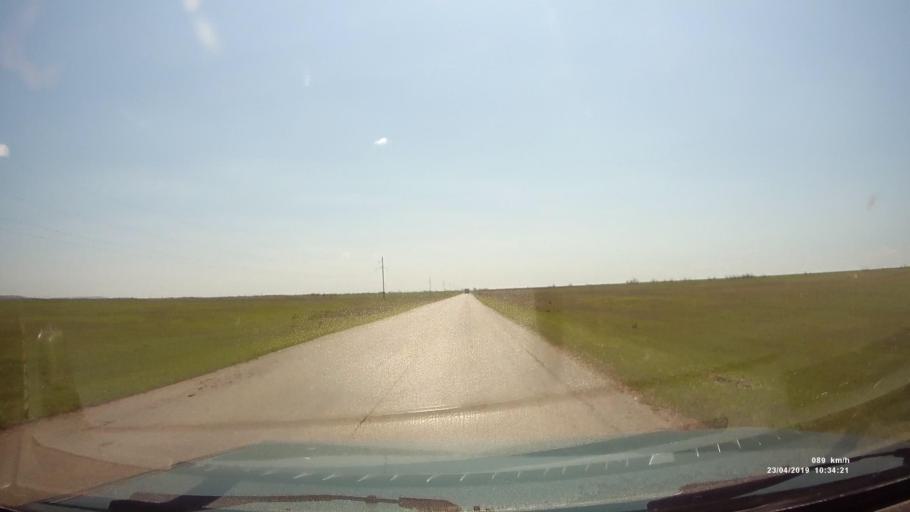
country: RU
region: Kalmykiya
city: Yashalta
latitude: 46.5649
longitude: 42.6091
